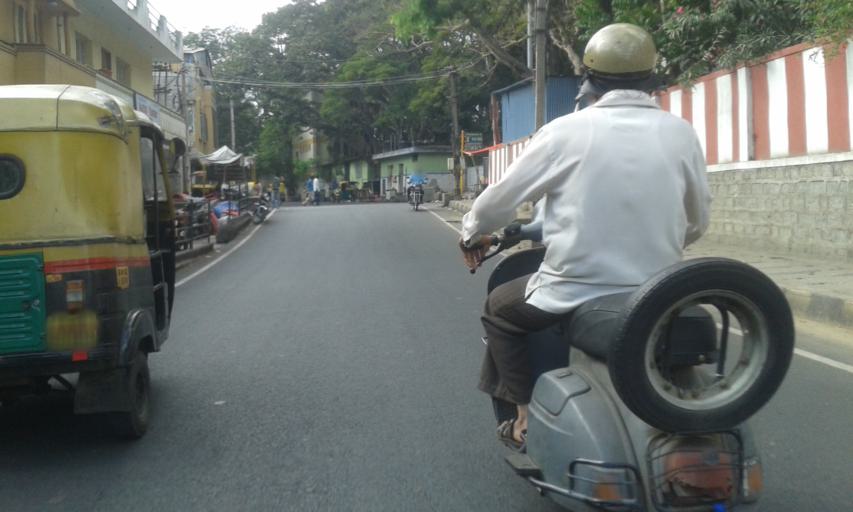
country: IN
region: Karnataka
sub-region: Bangalore Urban
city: Bangalore
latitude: 12.9324
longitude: 77.5899
